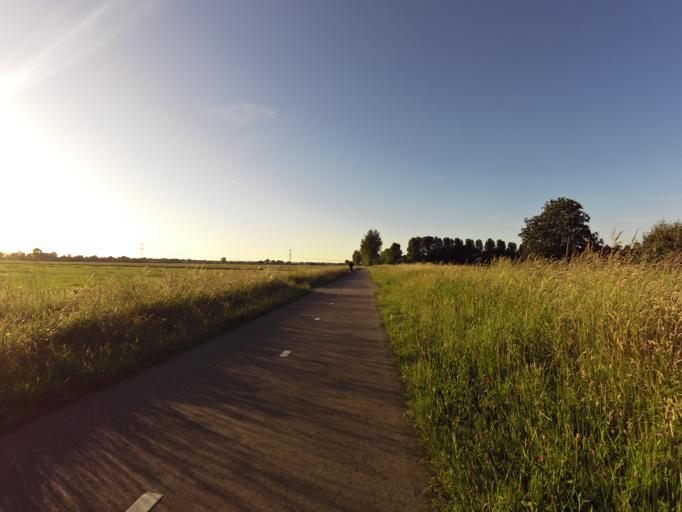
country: NL
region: Gelderland
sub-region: Gemeente Zevenaar
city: Zevenaar
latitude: 51.9476
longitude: 6.0839
